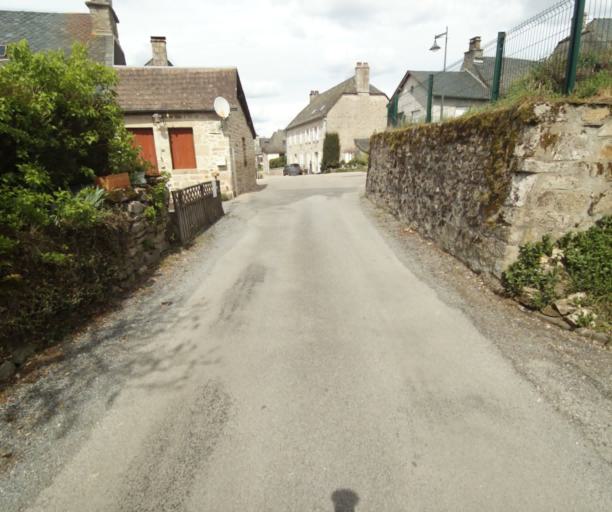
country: FR
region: Limousin
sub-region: Departement de la Correze
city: Laguenne
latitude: 45.2186
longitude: 1.8951
